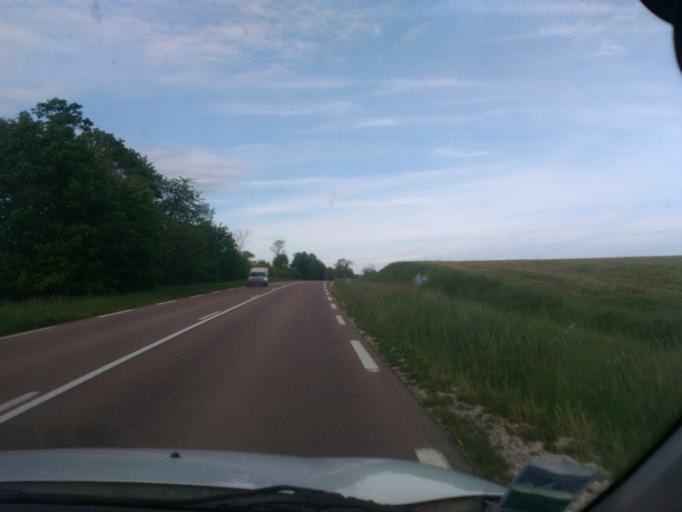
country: FR
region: Champagne-Ardenne
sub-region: Departement de l'Aube
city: Bar-sur-Aube
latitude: 48.2618
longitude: 4.5992
